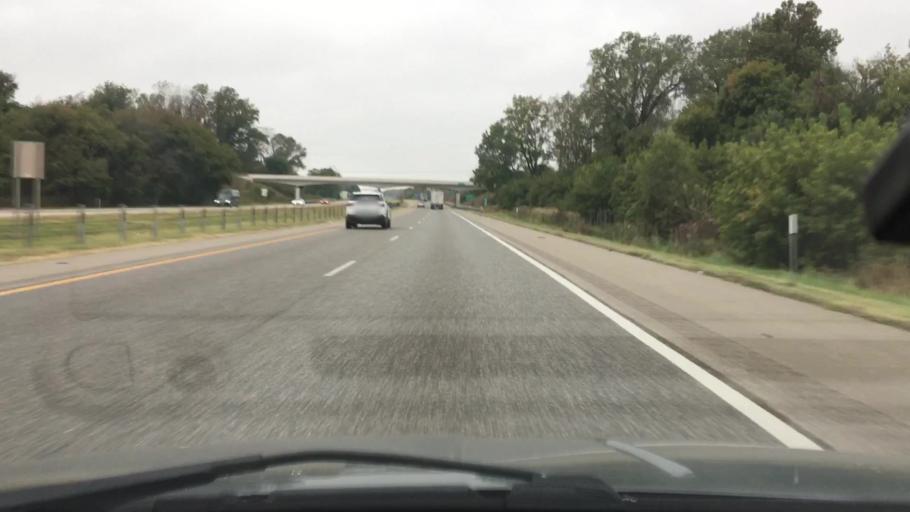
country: US
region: Michigan
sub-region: Van Buren County
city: Hartford
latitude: 42.1938
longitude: -86.1444
